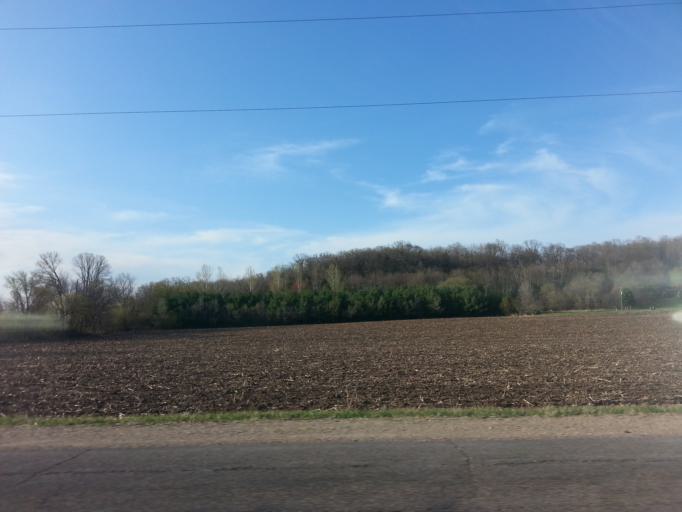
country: US
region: Wisconsin
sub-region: Pierce County
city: River Falls
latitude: 44.8625
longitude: -92.6998
